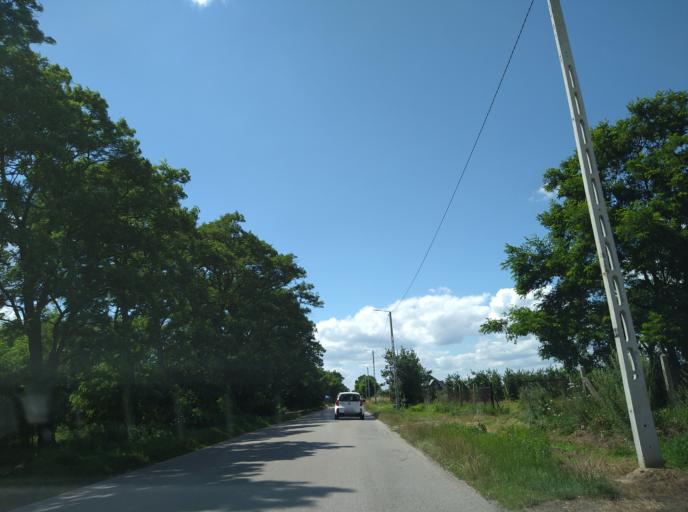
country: PL
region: Masovian Voivodeship
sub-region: Powiat bialobrzeski
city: Bialobrzegi
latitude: 51.6710
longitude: 20.9090
